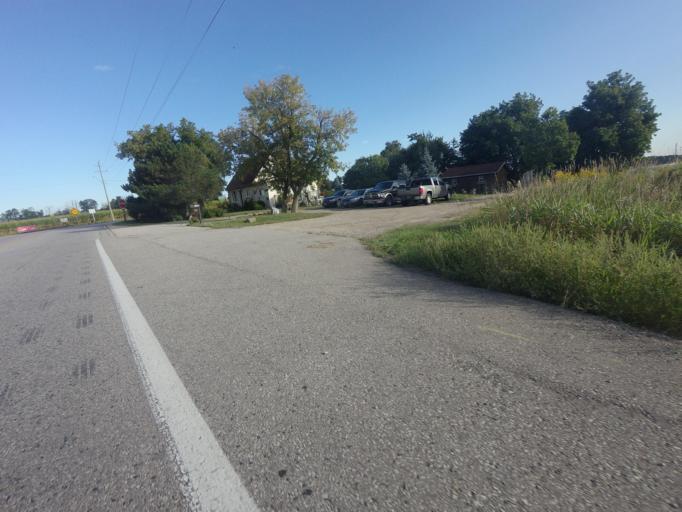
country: CA
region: Ontario
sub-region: Wellington County
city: Guelph
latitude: 43.5896
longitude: -80.3490
